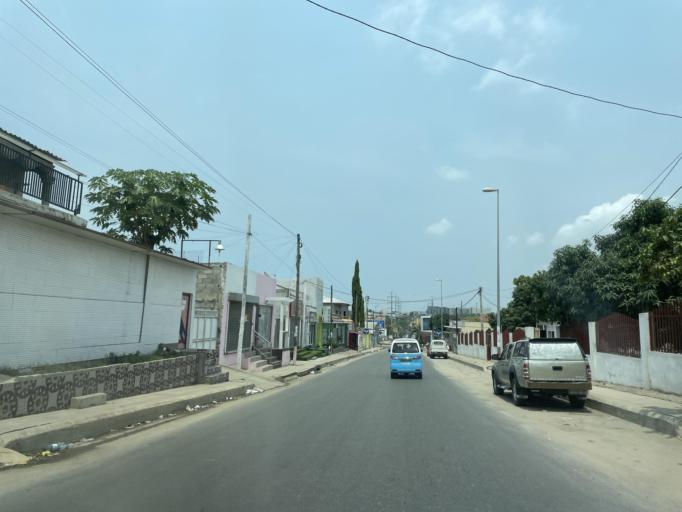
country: AO
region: Luanda
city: Luanda
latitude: -8.9356
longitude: 13.1708
